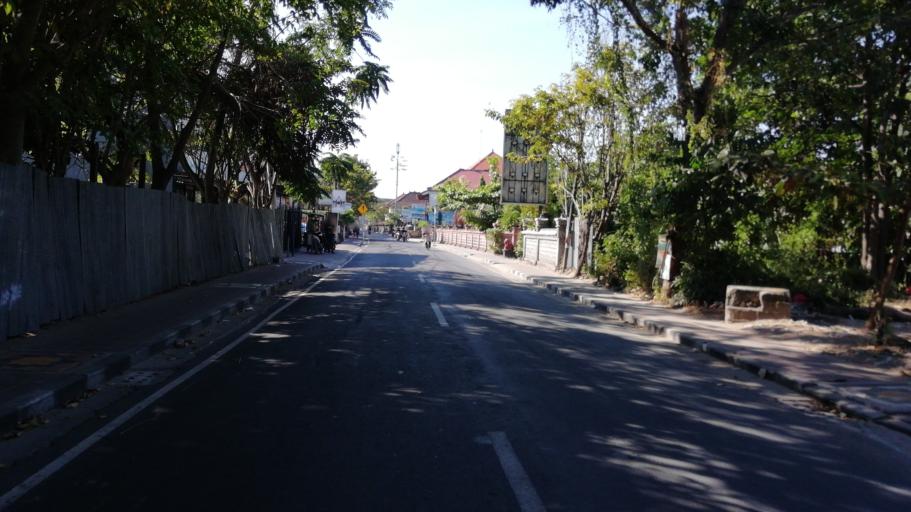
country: ID
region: Bali
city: Bualu
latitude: -8.7628
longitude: 115.2221
